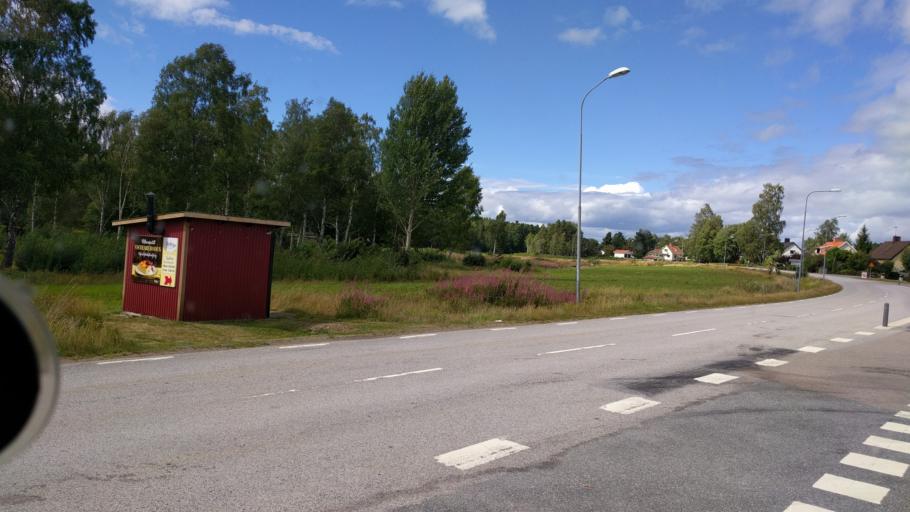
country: SE
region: Kalmar
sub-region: Vimmerby Kommun
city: Vimmerby
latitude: 57.6980
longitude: 16.0038
